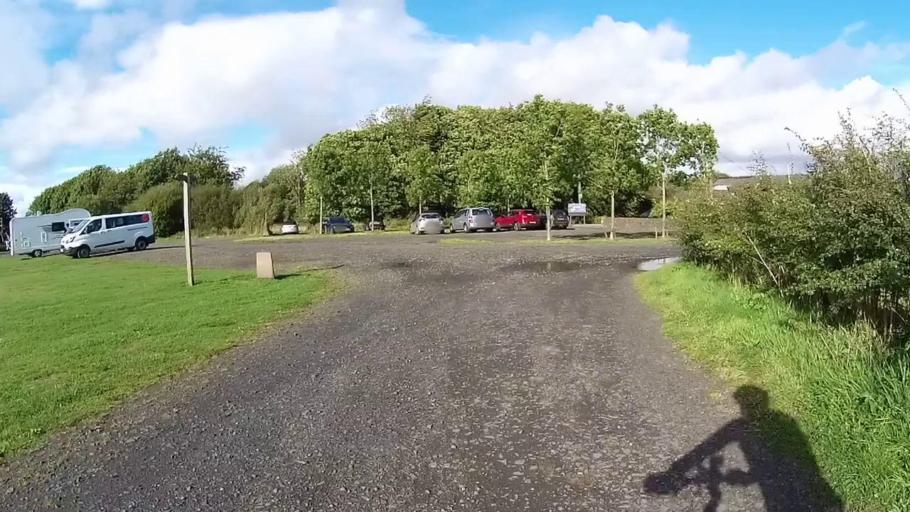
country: GB
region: Scotland
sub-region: Perth and Kinross
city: Kinross
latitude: 56.1996
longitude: -3.4172
